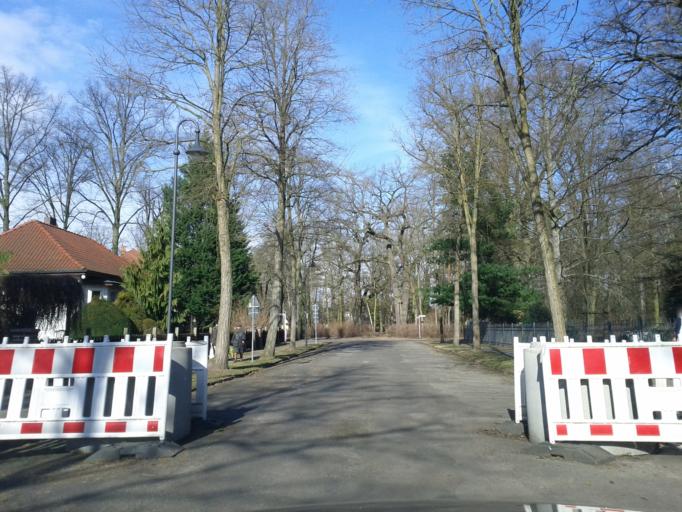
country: DE
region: Brandenburg
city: Schoneiche
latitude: 52.4692
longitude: 13.6894
